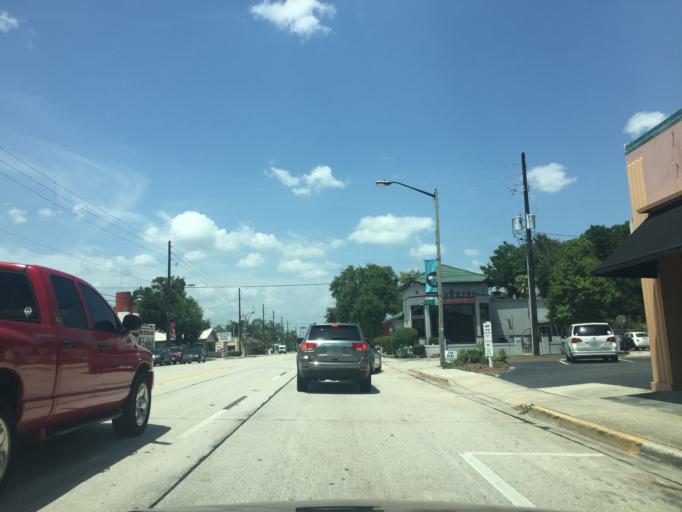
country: US
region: Florida
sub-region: Orange County
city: Orlando
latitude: 28.5601
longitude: -81.3644
